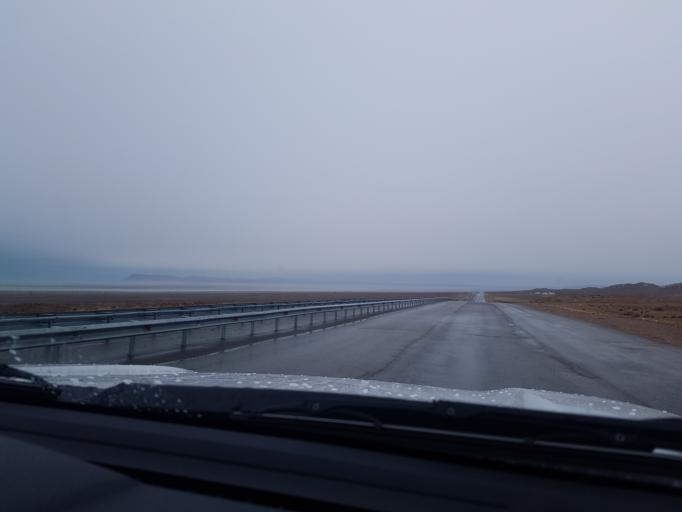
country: TM
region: Balkan
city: Turkmenbasy
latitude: 40.0294
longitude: 53.5003
